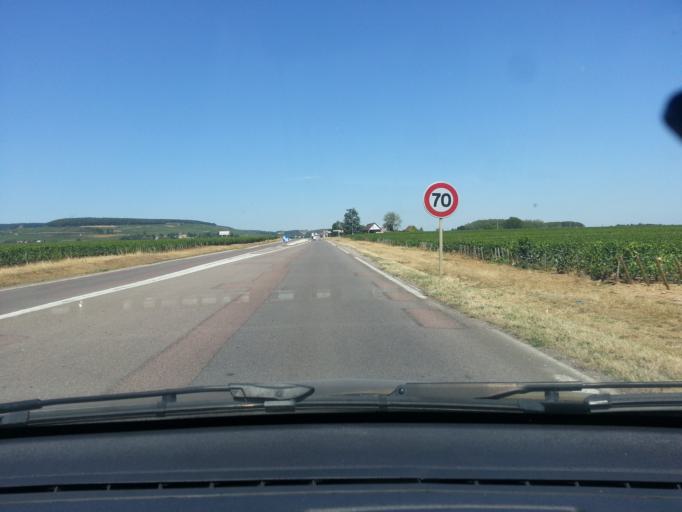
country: FR
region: Bourgogne
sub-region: Departement de la Cote-d'Or
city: Beaune
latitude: 47.0472
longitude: 4.8527
